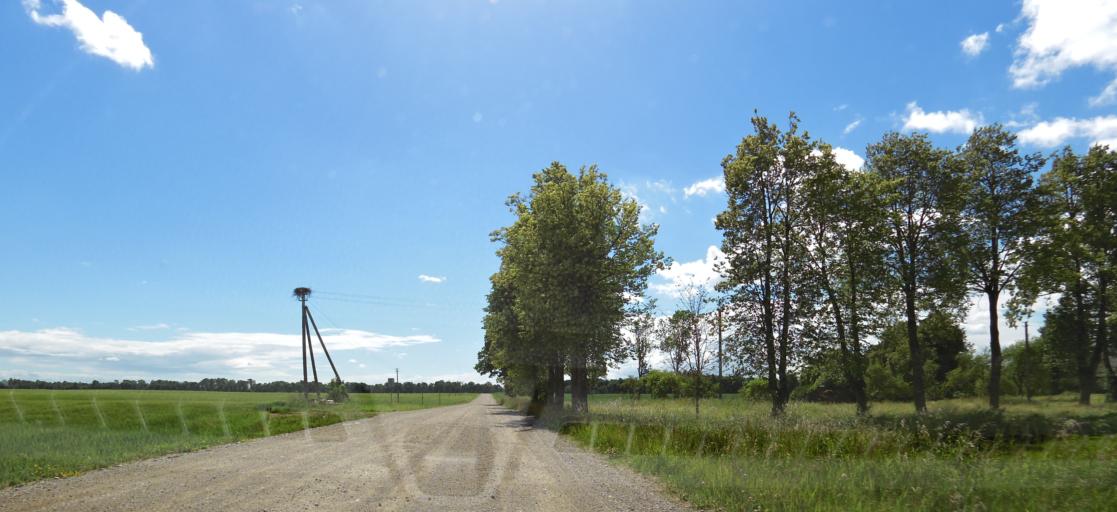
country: LT
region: Panevezys
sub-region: Birzai
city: Birzai
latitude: 56.3796
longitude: 24.7021
